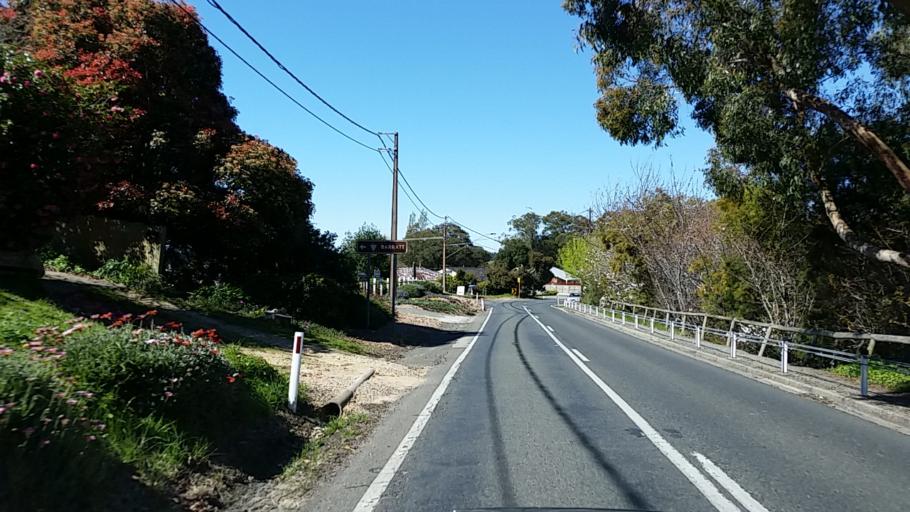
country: AU
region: South Australia
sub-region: Adelaide Hills
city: Bridgewater
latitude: -34.9590
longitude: 138.7360
